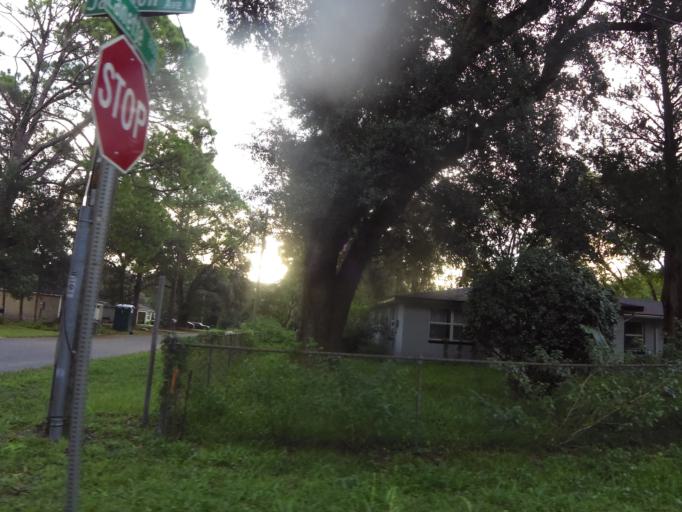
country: US
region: Florida
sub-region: Duval County
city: Jacksonville
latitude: 30.3326
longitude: -81.7861
